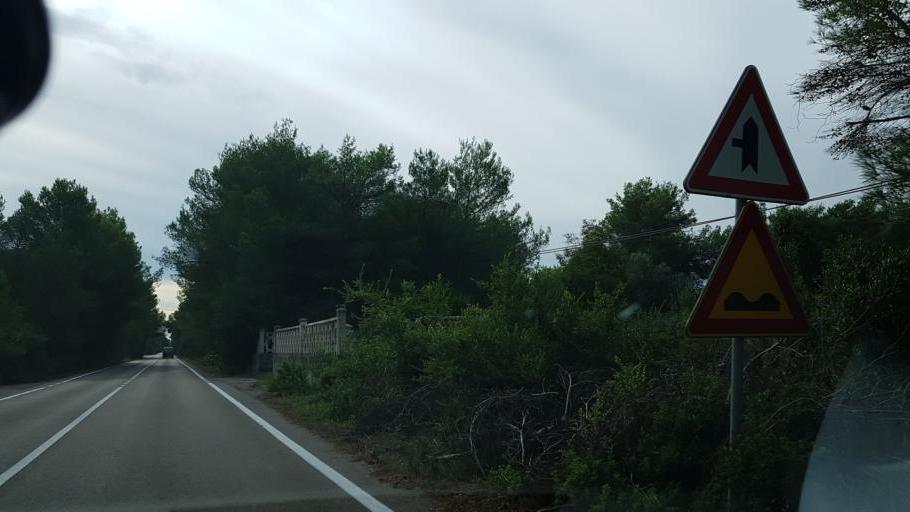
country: IT
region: Apulia
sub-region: Provincia di Lecce
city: Struda
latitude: 40.3710
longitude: 18.3076
